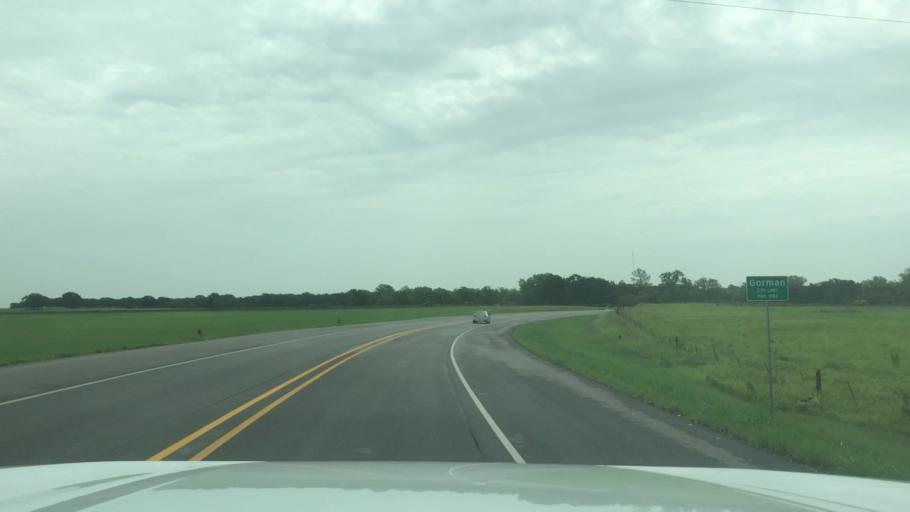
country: US
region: Texas
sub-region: Eastland County
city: Gorman
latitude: 32.2217
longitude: -98.6813
